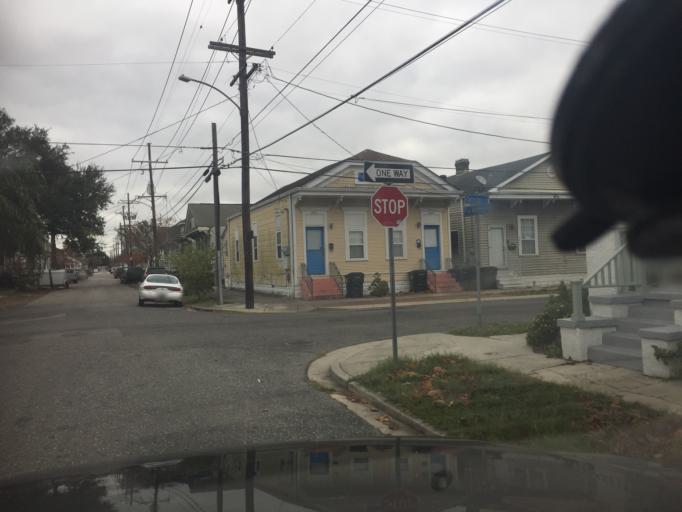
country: US
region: Louisiana
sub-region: Orleans Parish
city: New Orleans
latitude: 29.9807
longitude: -90.0757
